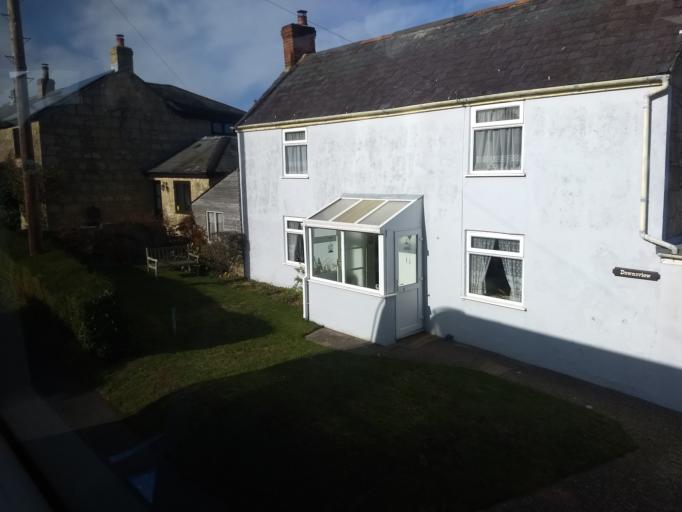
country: GB
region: England
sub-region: Isle of Wight
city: Shalfleet
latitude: 50.6862
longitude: -1.4185
